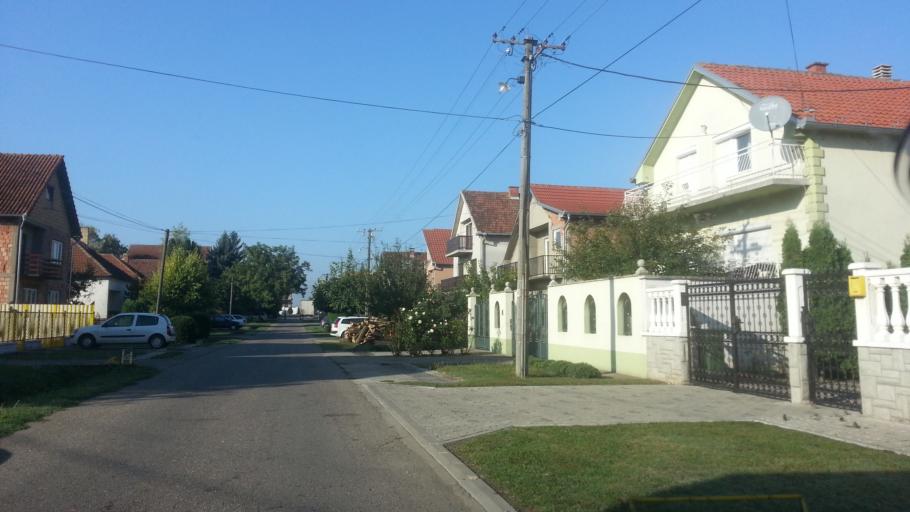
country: RS
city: Stari Banovci
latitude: 44.9805
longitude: 20.2746
